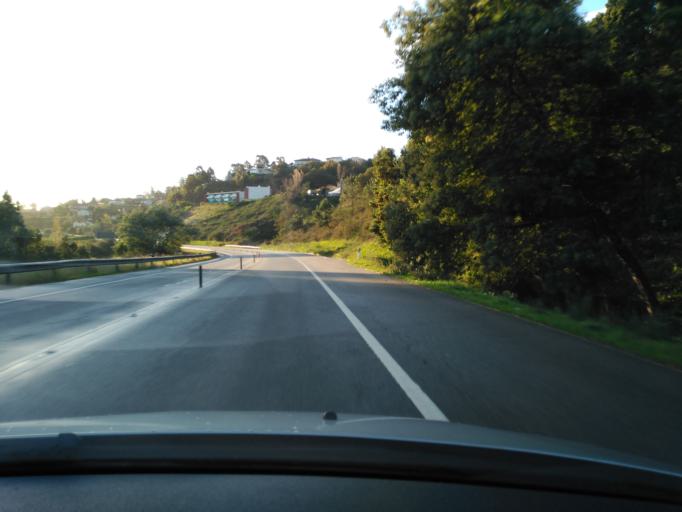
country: PT
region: Braga
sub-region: Guimaraes
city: Guimaraes
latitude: 41.4479
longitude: -8.2572
